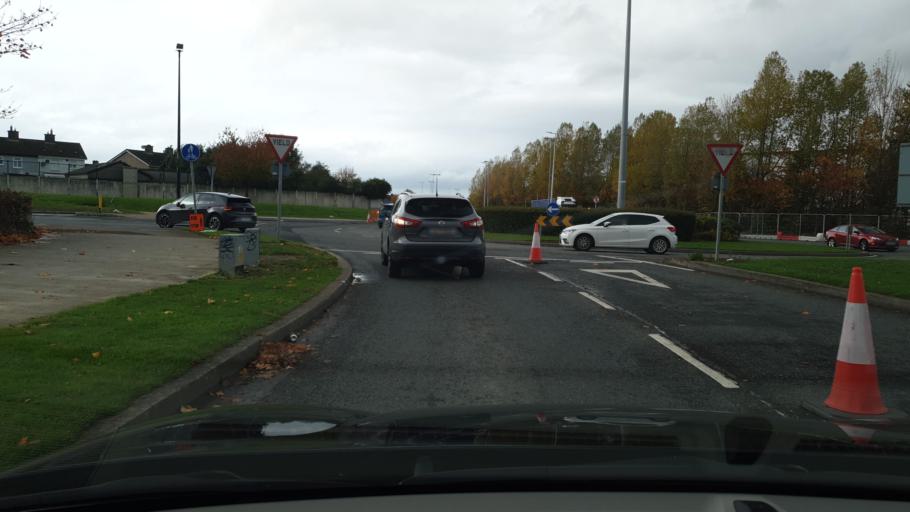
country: IE
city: Palmerstown
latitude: 53.3504
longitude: -6.3927
